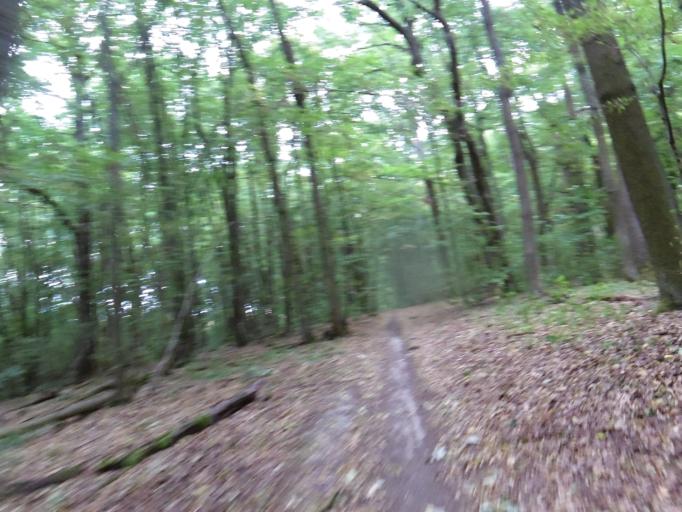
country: DE
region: Bavaria
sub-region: Regierungsbezirk Unterfranken
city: Waldbuttelbrunn
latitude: 49.7776
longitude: 9.8535
